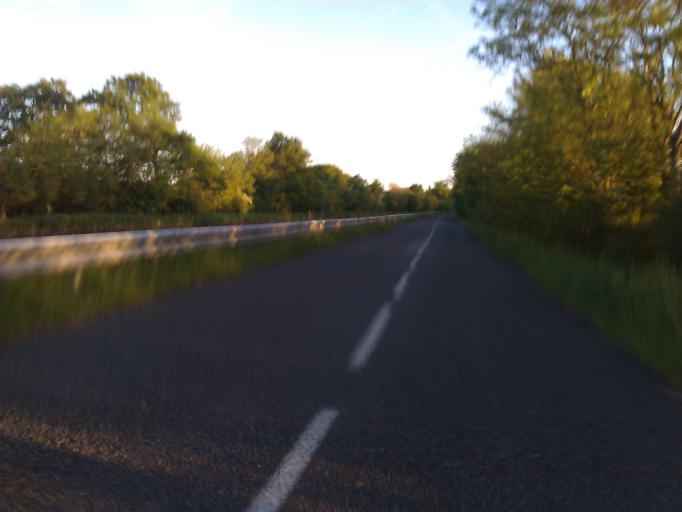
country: FR
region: Bourgogne
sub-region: Departement de Saone-et-Loire
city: Paray-le-Monial
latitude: 46.4759
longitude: 4.1722
